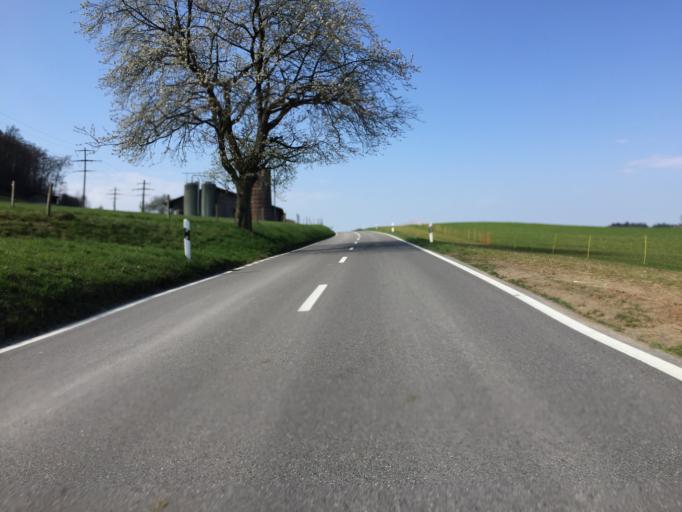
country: CH
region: Bern
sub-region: Bern-Mittelland District
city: Bolligen
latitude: 46.9885
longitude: 7.5112
